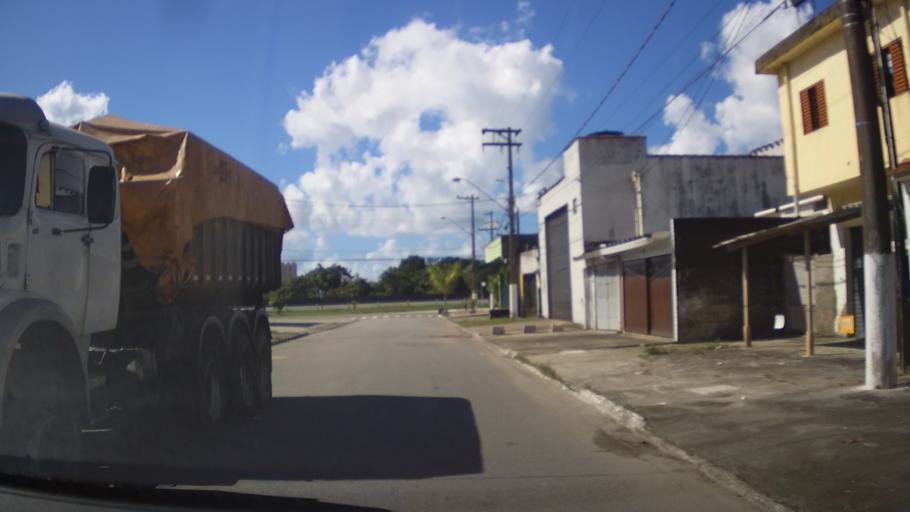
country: BR
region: Sao Paulo
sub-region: Praia Grande
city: Praia Grande
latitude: -24.0242
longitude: -46.5067
